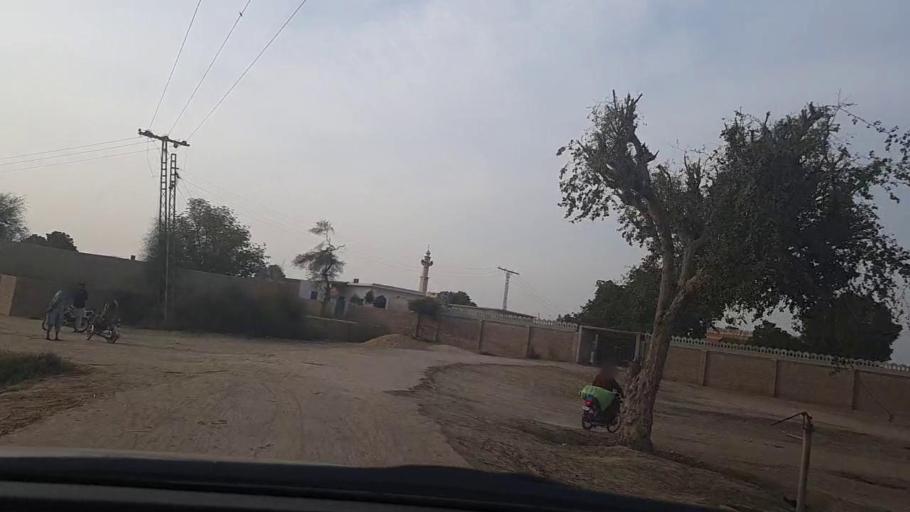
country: PK
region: Sindh
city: Daulatpur
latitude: 26.3374
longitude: 68.0200
